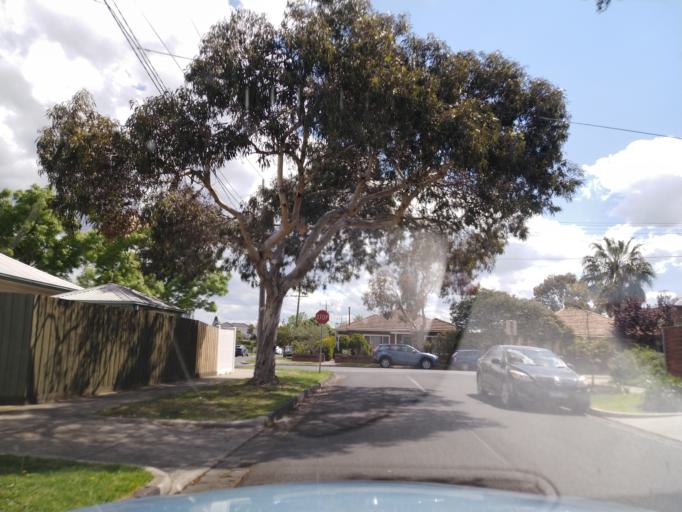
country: AU
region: Victoria
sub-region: Hobsons Bay
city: South Kingsville
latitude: -37.8386
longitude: 144.8651
